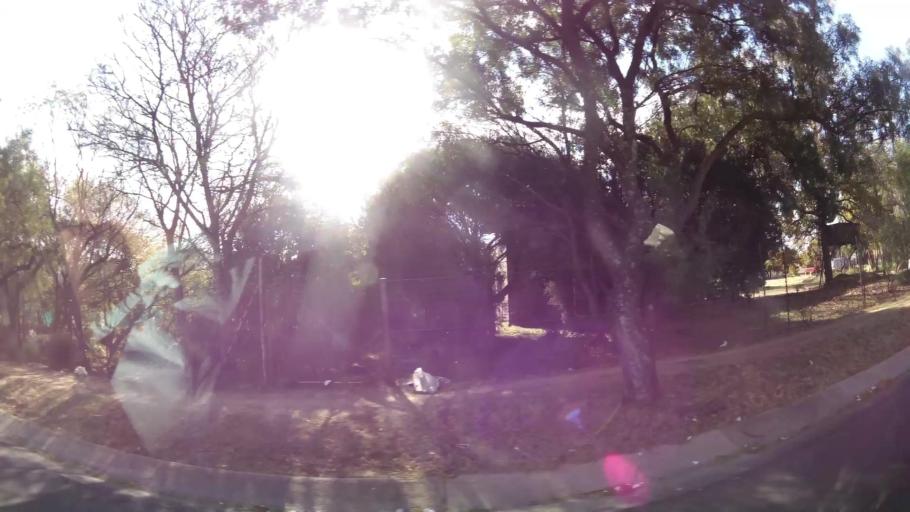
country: ZA
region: Gauteng
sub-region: City of Johannesburg Metropolitan Municipality
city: Midrand
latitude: -26.0154
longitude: 28.1570
